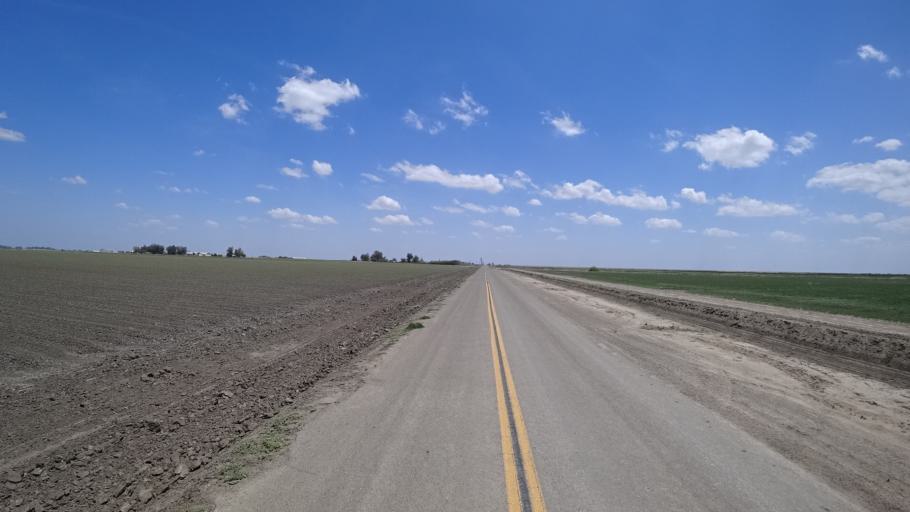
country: US
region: California
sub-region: Kings County
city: Stratford
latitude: 36.1527
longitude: -119.8243
